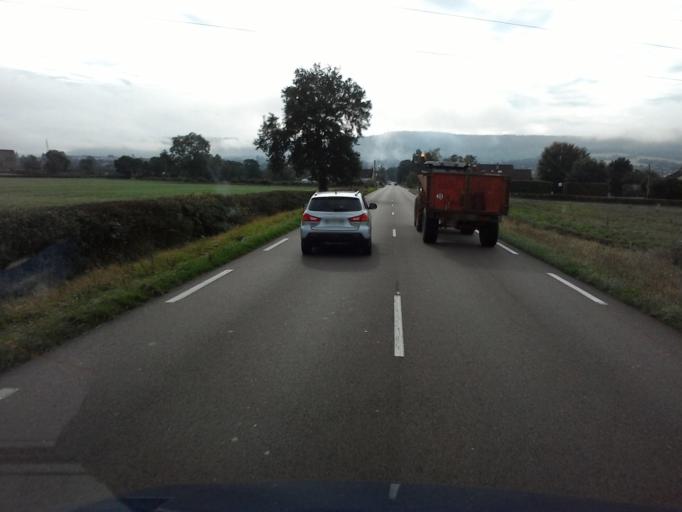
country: FR
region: Bourgogne
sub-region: Departement de Saone-et-Loire
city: Autun
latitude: 46.9631
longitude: 4.2801
